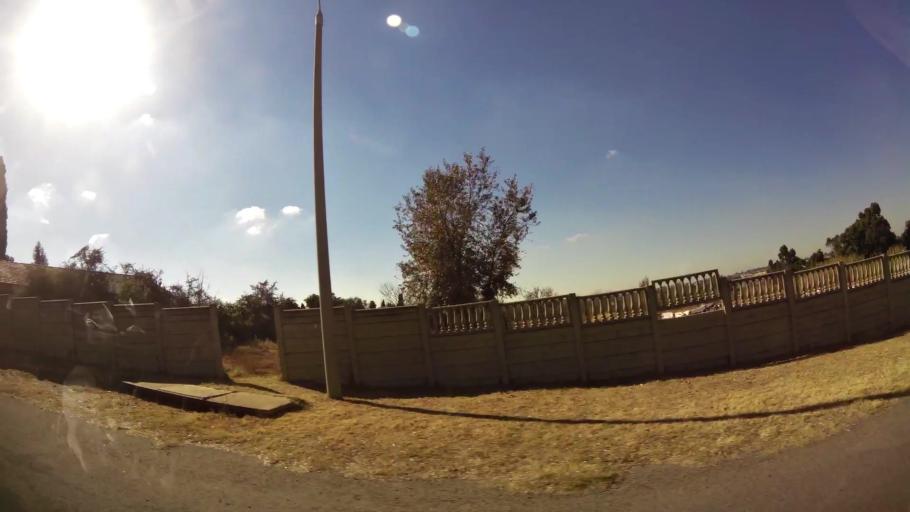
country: ZA
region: Gauteng
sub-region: City of Johannesburg Metropolitan Municipality
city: Roodepoort
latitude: -26.1488
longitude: 27.8372
